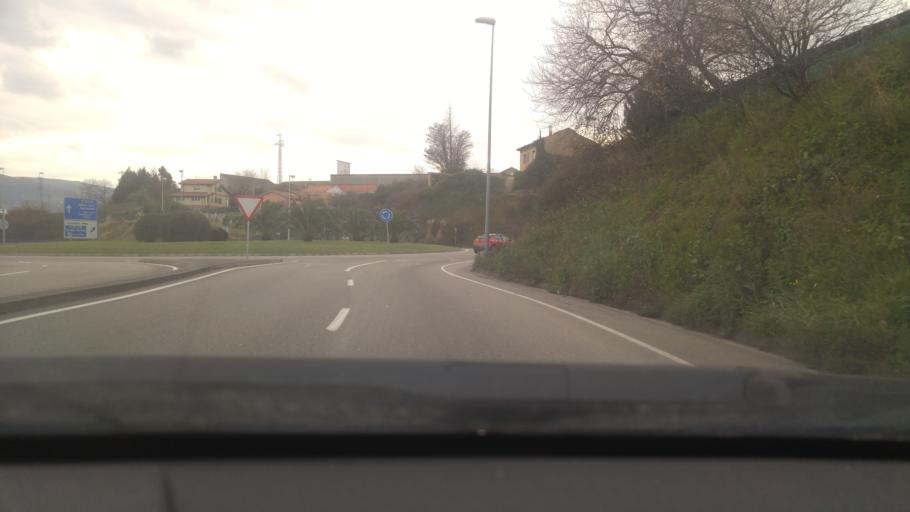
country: ES
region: Asturias
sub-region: Province of Asturias
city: Gijon
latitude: 43.5205
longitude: -5.6578
